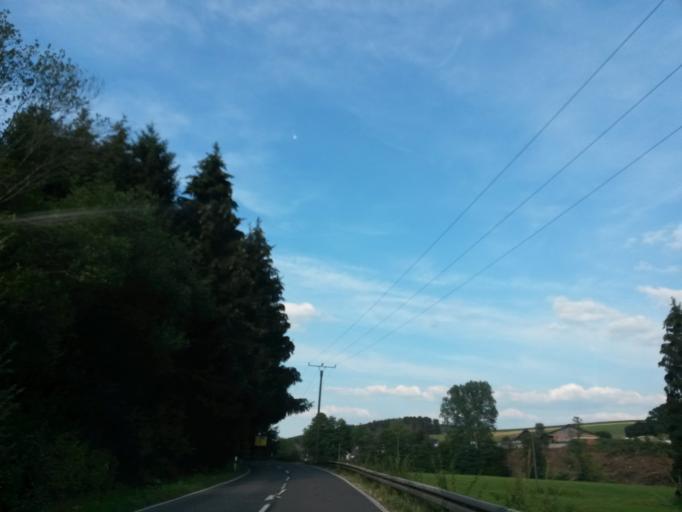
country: DE
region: North Rhine-Westphalia
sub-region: Regierungsbezirk Koln
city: Overath
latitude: 50.9883
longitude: 7.3180
